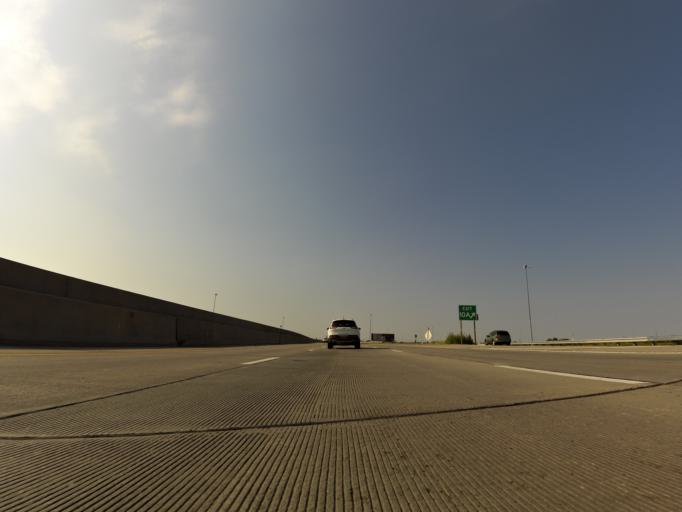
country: US
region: Kansas
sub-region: Sedgwick County
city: Wichita
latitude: 37.7365
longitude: -97.3174
